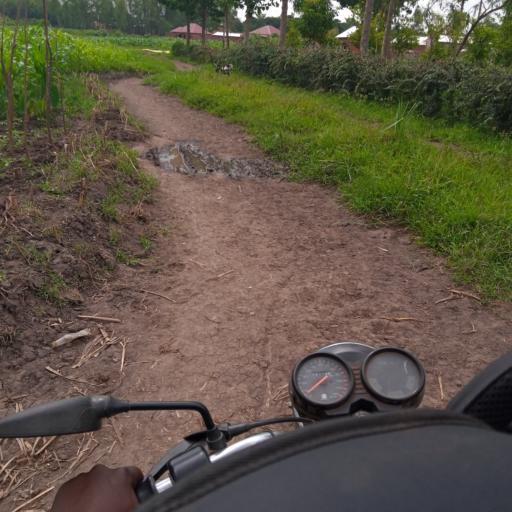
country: UG
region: Eastern Region
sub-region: Mbale District
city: Mbale
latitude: 1.1044
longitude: 34.1786
